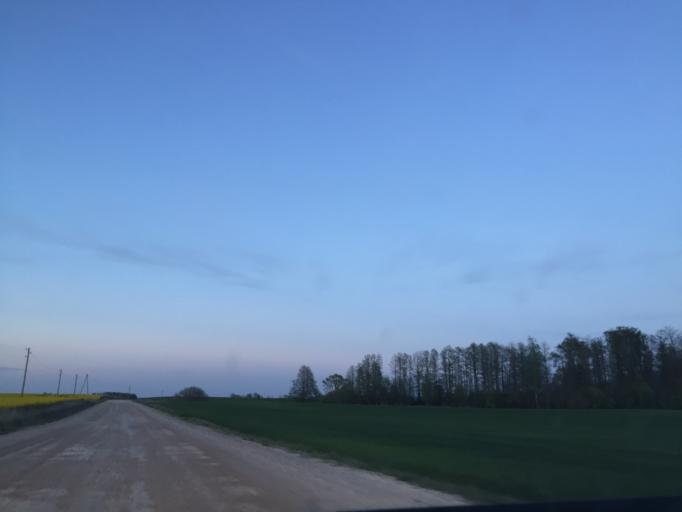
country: LV
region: Bauskas Rajons
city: Bauska
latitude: 56.4978
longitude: 24.1451
